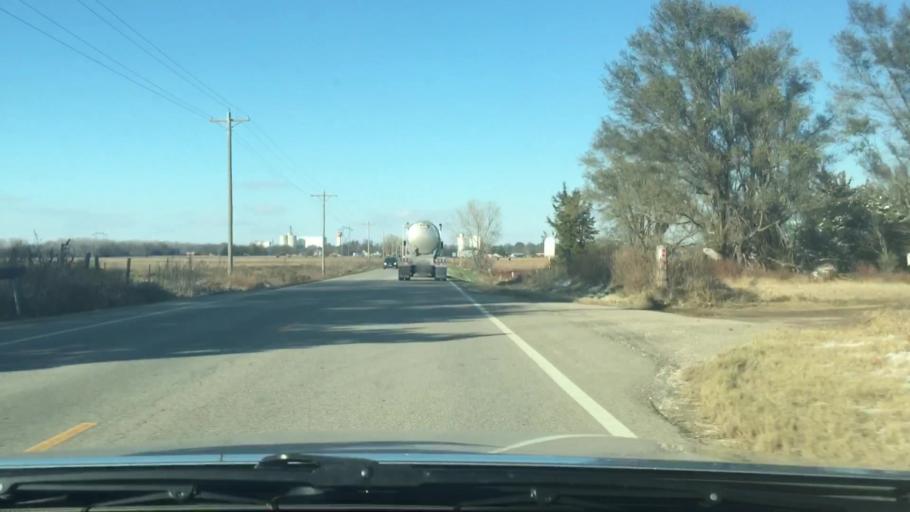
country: US
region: Kansas
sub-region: Rice County
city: Sterling
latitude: 38.1918
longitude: -98.2068
